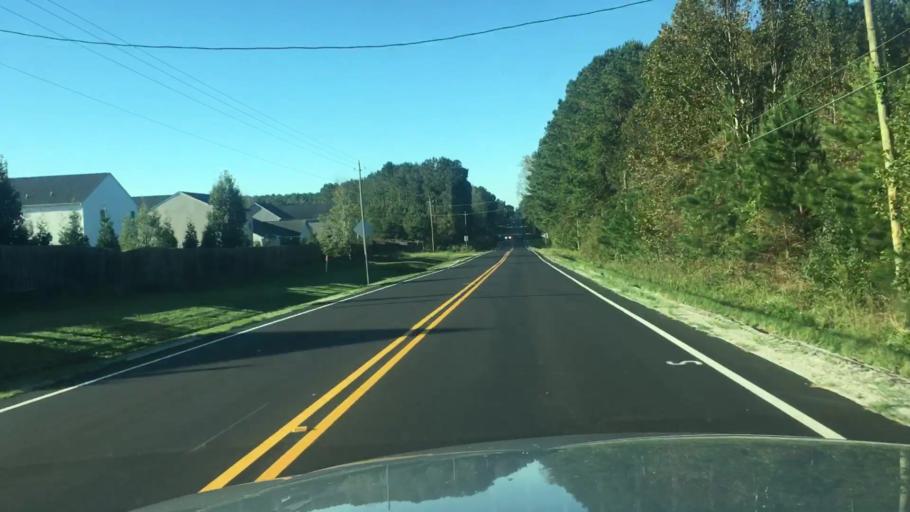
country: US
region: North Carolina
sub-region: Harnett County
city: Lillington
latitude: 35.3453
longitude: -78.8525
